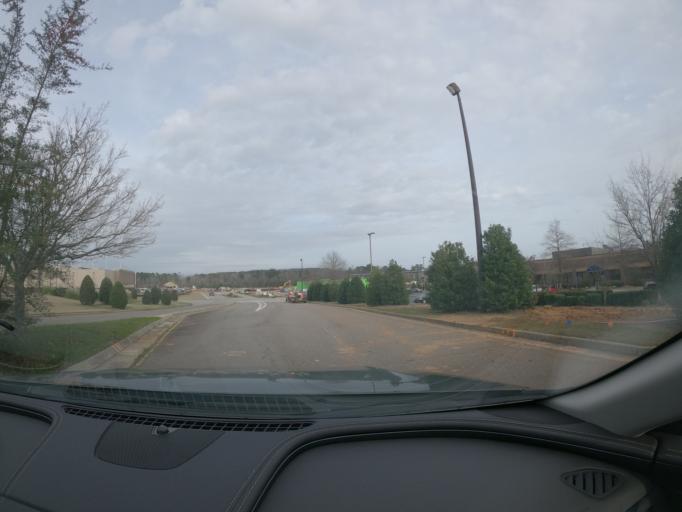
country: US
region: South Carolina
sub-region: Aiken County
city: North Augusta
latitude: 33.5225
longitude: -82.0174
